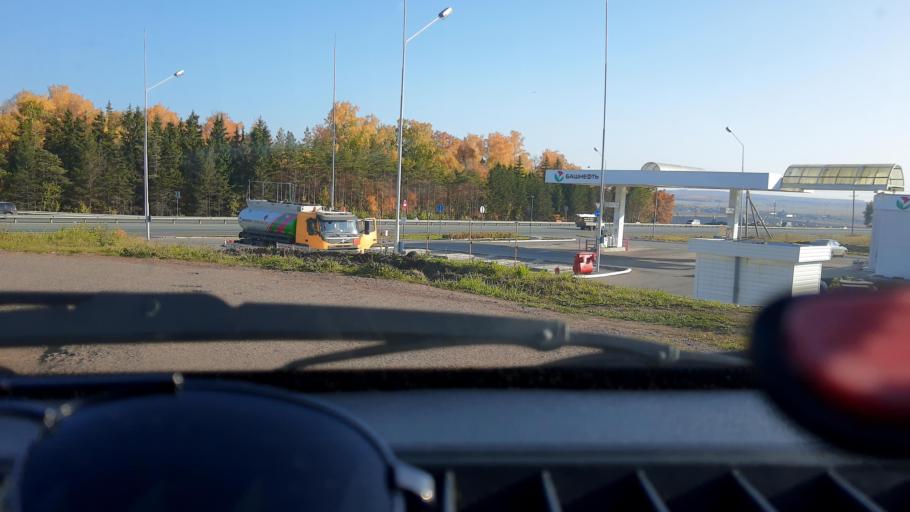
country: RU
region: Bashkortostan
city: Karmaskaly
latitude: 54.3761
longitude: 55.9156
